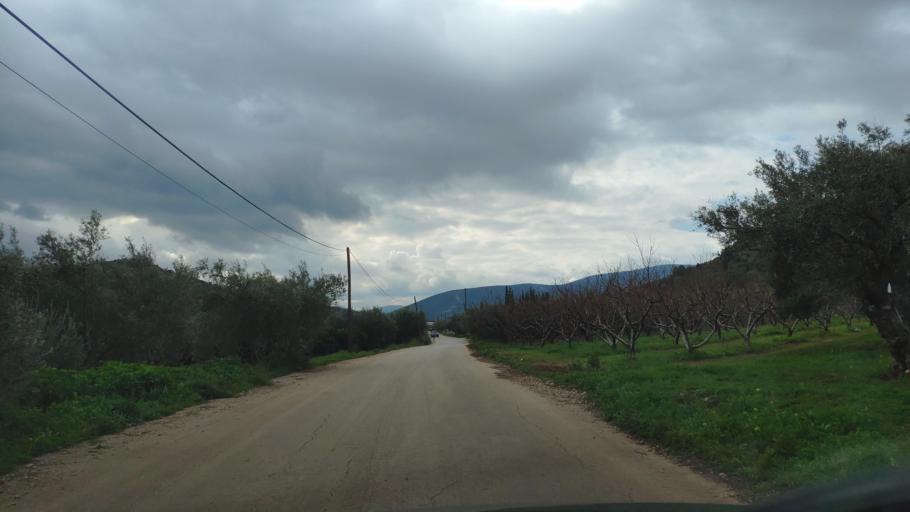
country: GR
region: Peloponnese
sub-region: Nomos Argolidos
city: Nea Kios
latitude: 37.5452
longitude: 22.7126
